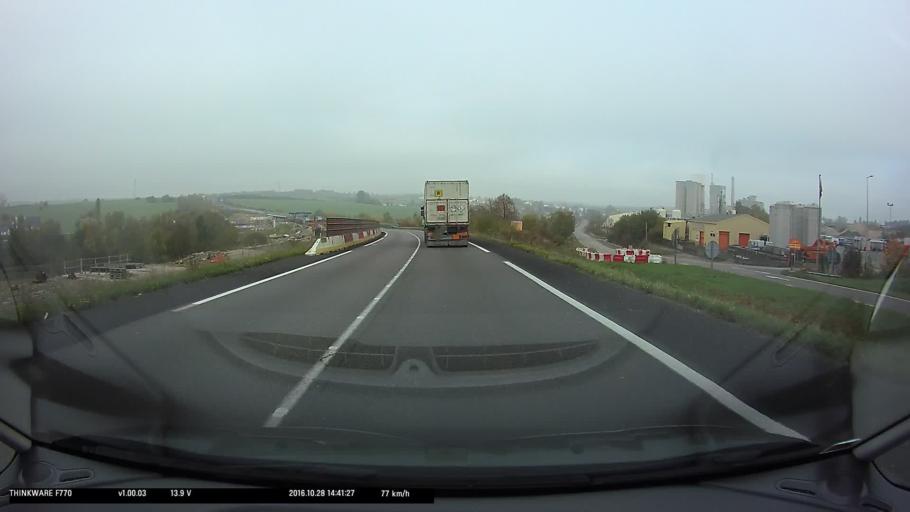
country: FR
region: Lorraine
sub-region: Departement de la Moselle
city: Lorquin
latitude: 48.6859
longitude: 6.9574
